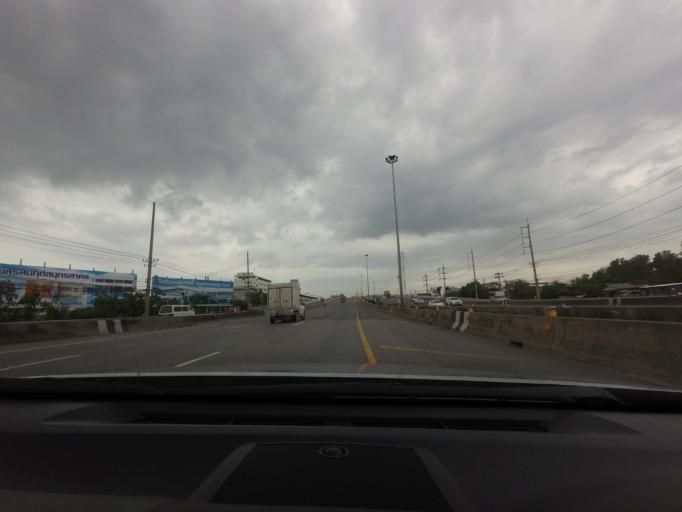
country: TH
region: Samut Sakhon
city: Samut Sakhon
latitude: 13.5431
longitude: 100.2547
